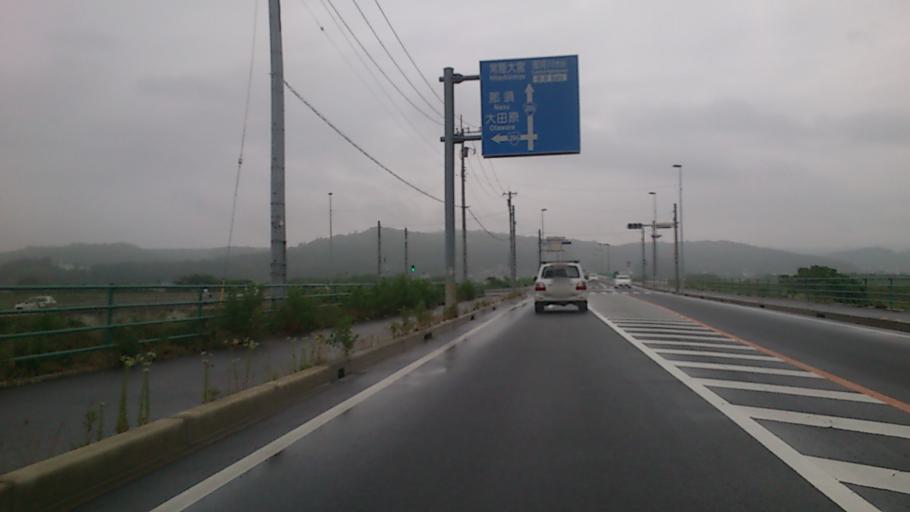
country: JP
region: Tochigi
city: Karasuyama
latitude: 36.7509
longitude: 140.1351
